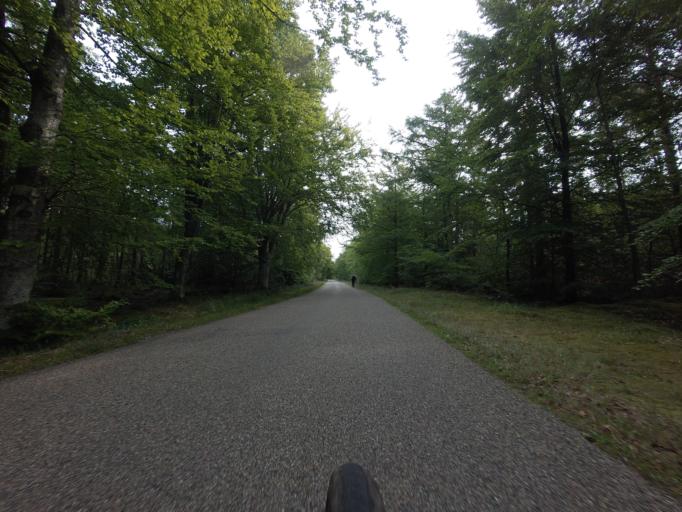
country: DK
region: North Denmark
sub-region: Hjorring Kommune
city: Hirtshals
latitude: 57.5793
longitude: 10.0664
